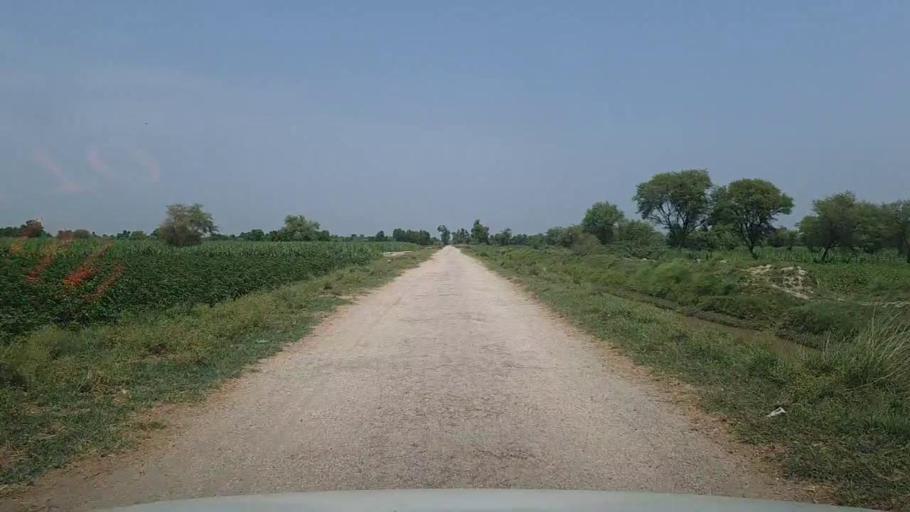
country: PK
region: Sindh
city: Karaundi
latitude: 26.8867
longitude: 68.3339
